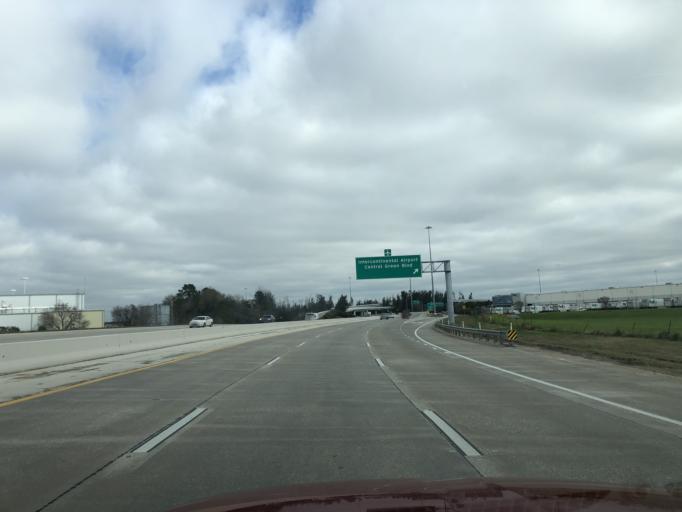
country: US
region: Texas
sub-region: Harris County
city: Aldine
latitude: 29.9541
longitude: -95.3835
